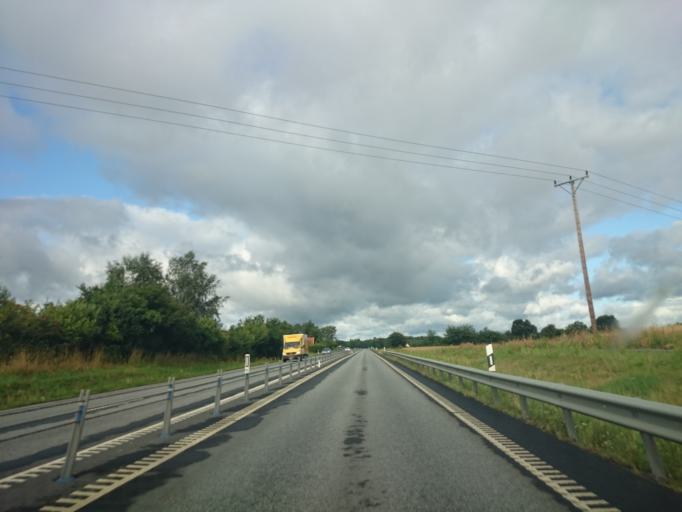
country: SE
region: Skane
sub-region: Kristianstads Kommun
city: Onnestad
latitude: 55.9329
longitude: 14.0142
